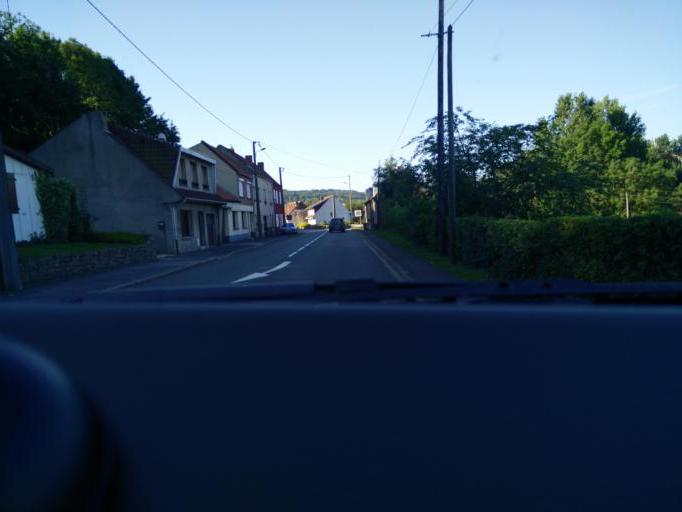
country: FR
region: Nord-Pas-de-Calais
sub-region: Departement du Pas-de-Calais
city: Divion
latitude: 50.4587
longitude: 2.4827
